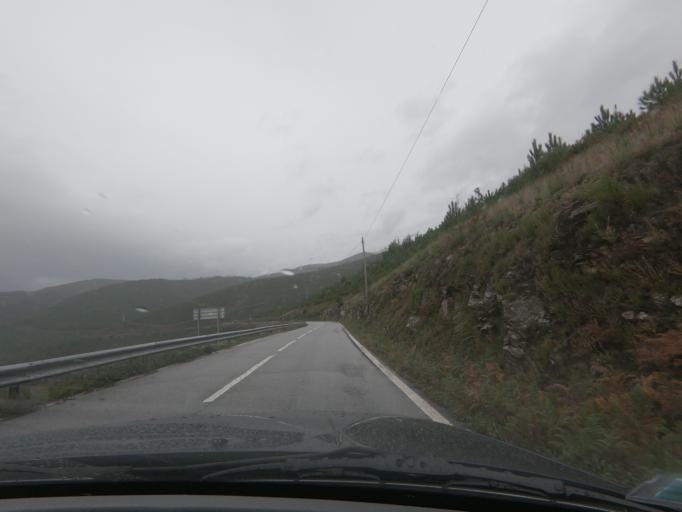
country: PT
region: Vila Real
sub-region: Mondim de Basto
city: Mondim de Basto
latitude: 41.3530
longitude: -7.9177
